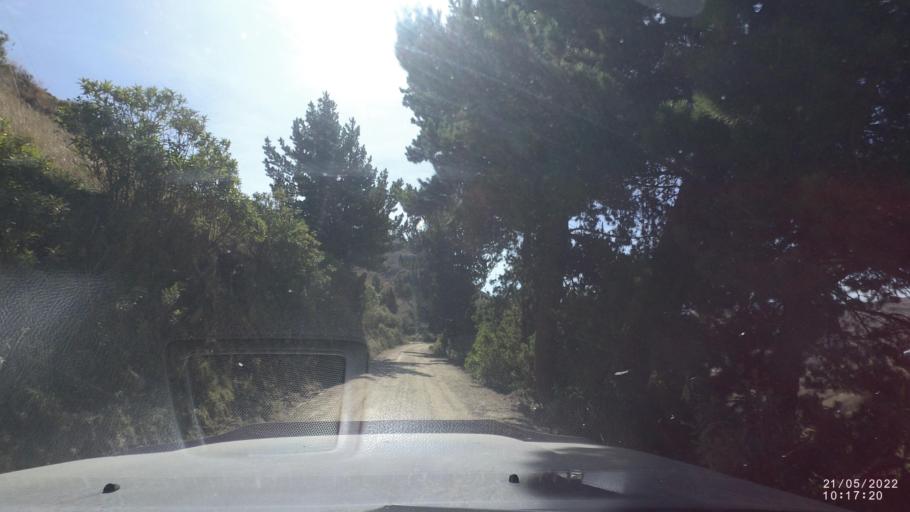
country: BO
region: Cochabamba
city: Colomi
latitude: -17.3296
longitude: -65.9636
